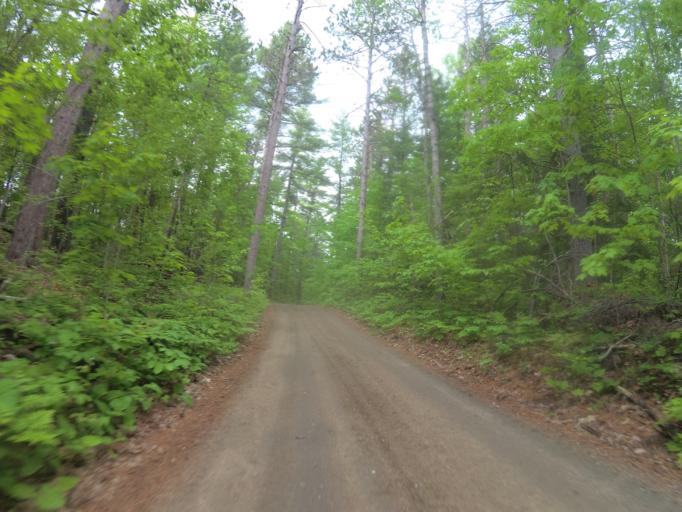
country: CA
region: Ontario
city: Renfrew
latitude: 45.1091
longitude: -76.8236
